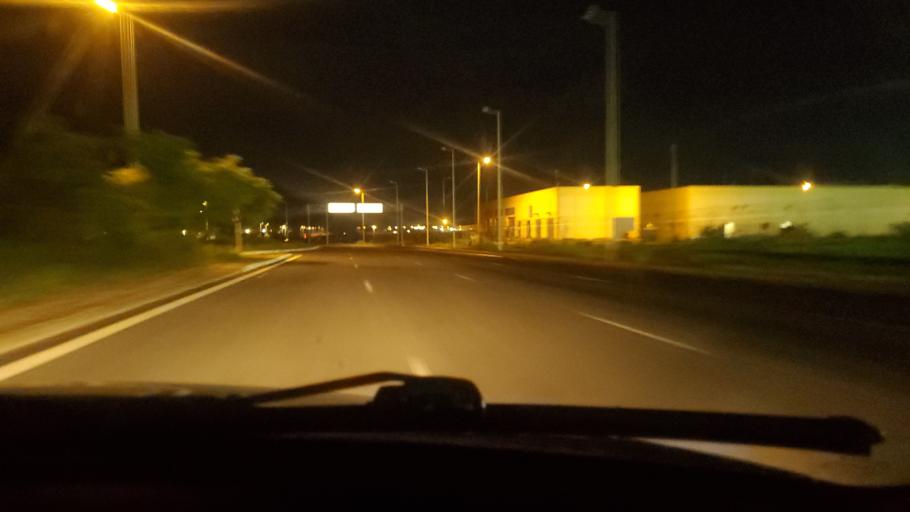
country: SN
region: Thies
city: Pout
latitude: 14.6669
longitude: -17.0657
